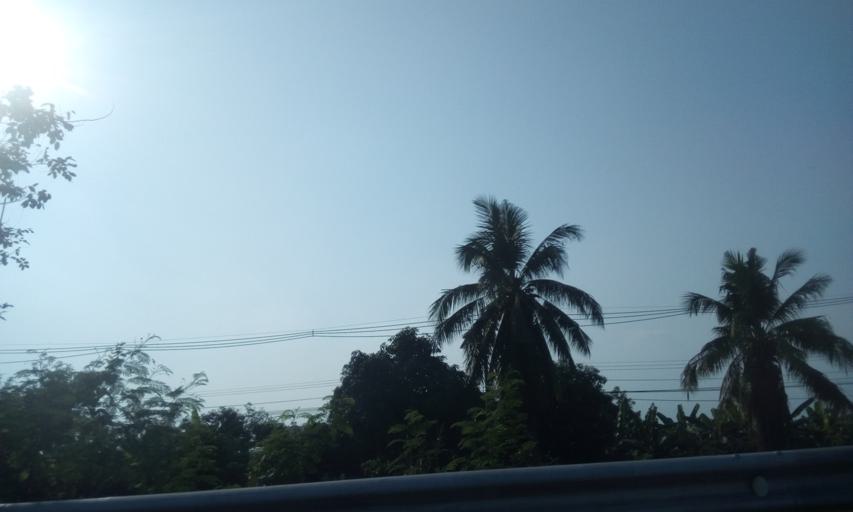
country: TH
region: Sing Buri
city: Phrom Buri
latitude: 14.8228
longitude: 100.4286
